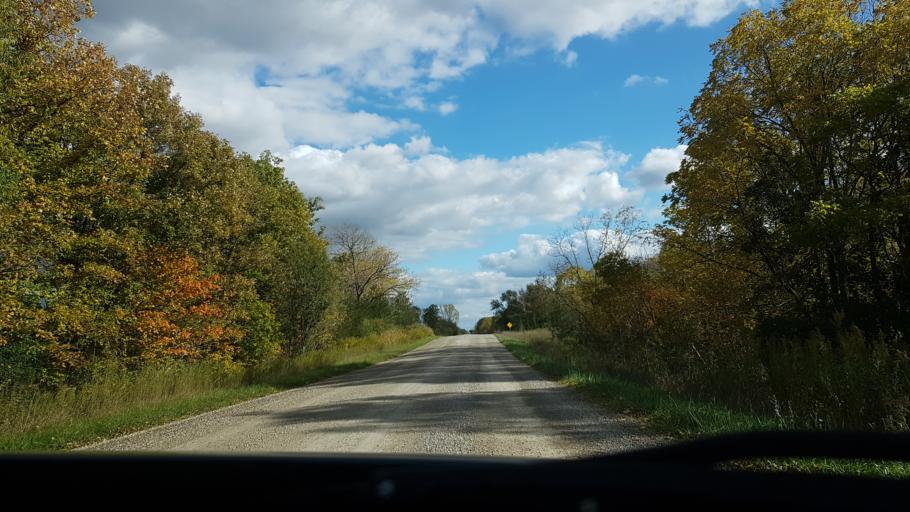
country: CA
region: Ontario
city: South Huron
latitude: 43.0885
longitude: -81.5842
